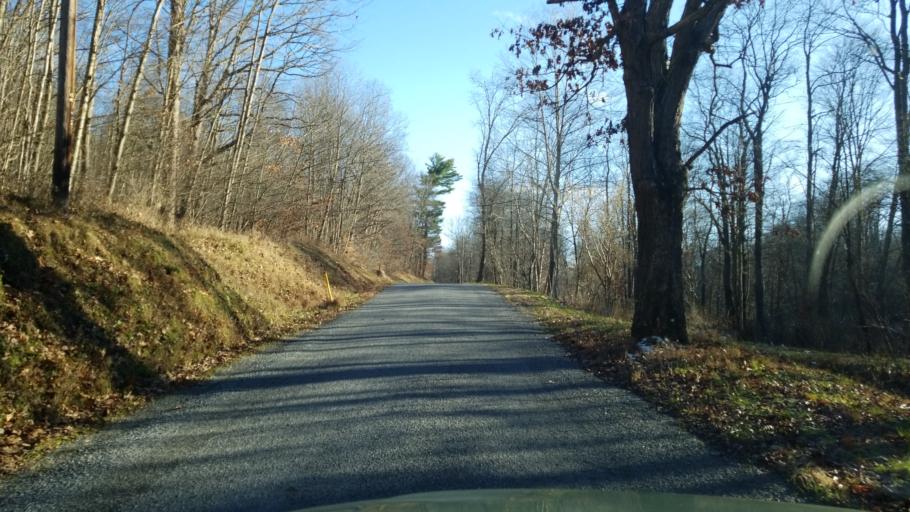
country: US
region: Pennsylvania
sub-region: Jefferson County
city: Brockway
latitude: 41.2775
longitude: -78.8167
